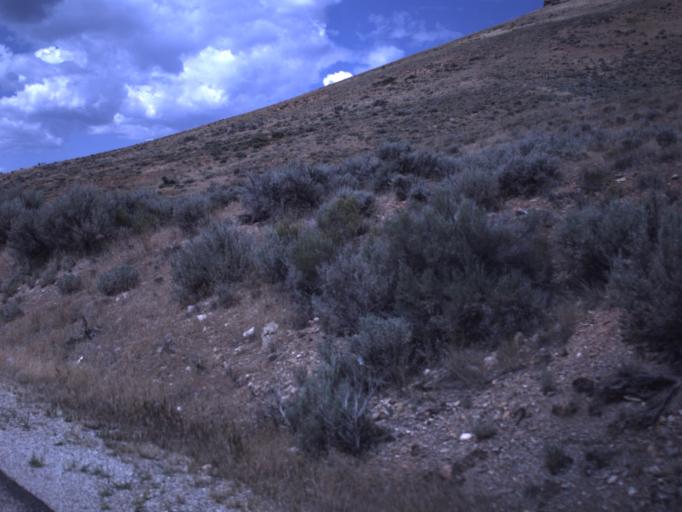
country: US
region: Utah
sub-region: Rich County
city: Randolph
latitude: 41.7684
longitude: -111.1663
